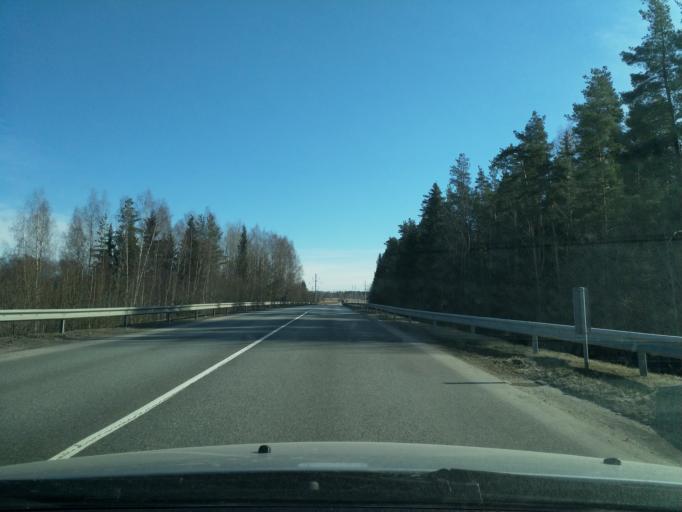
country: LV
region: Valmieras Rajons
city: Valmiera
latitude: 57.5103
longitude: 25.4377
